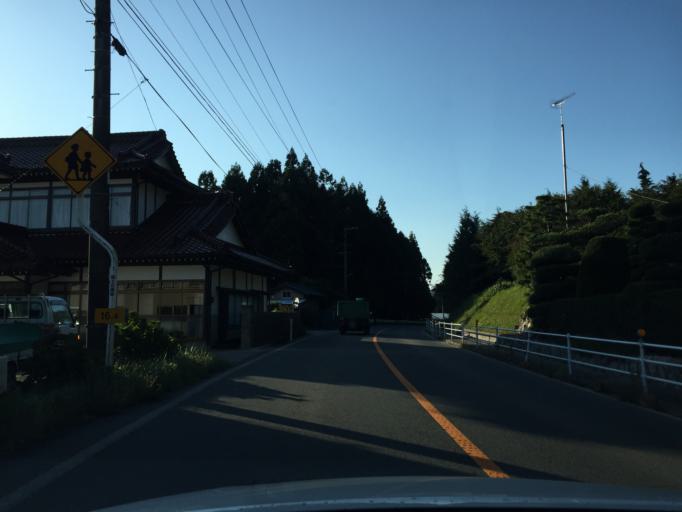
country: JP
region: Fukushima
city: Iwaki
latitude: 37.1125
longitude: 140.7581
